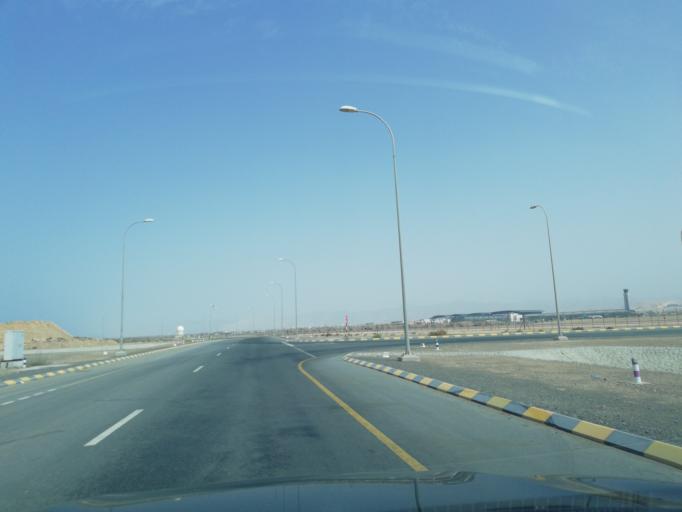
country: OM
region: Muhafazat Masqat
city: As Sib al Jadidah
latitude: 23.6161
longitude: 58.2750
